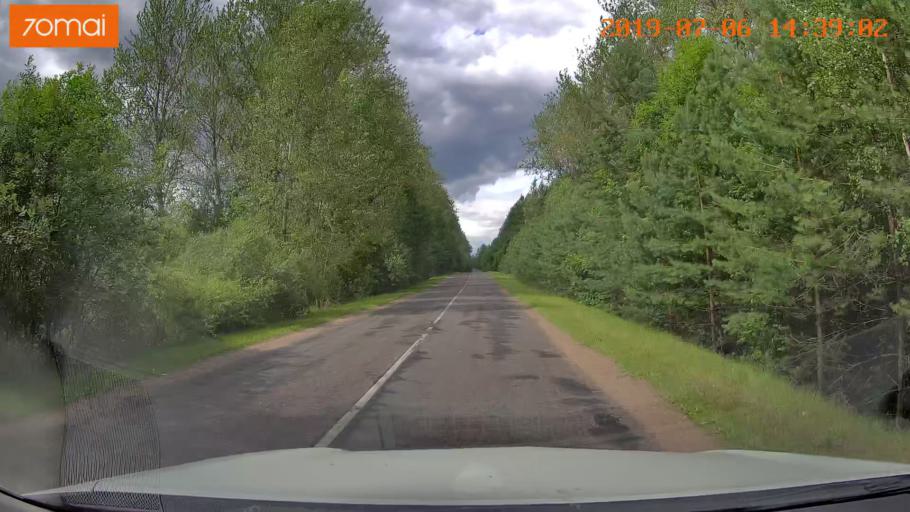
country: BY
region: Minsk
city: Ivyanyets
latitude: 53.9124
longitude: 26.6946
